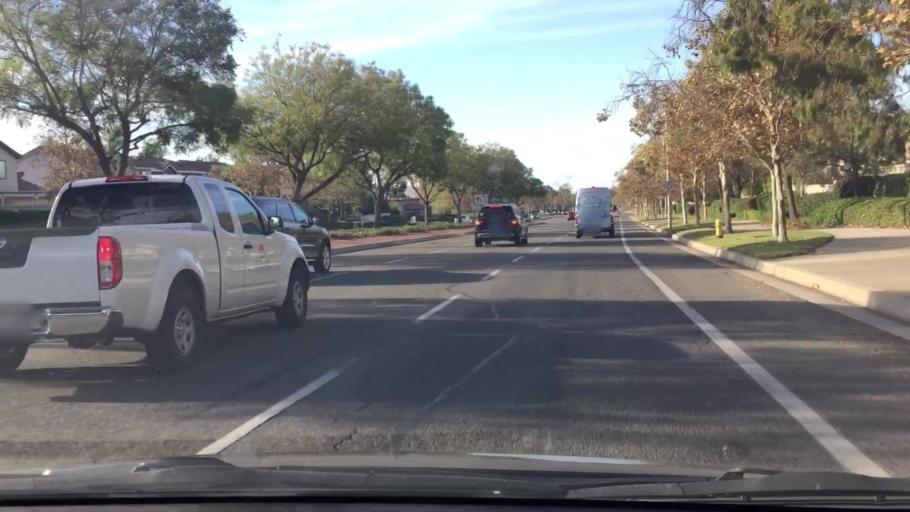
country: US
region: California
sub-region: Orange County
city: Rancho Santa Margarita
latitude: 33.6221
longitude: -117.6097
